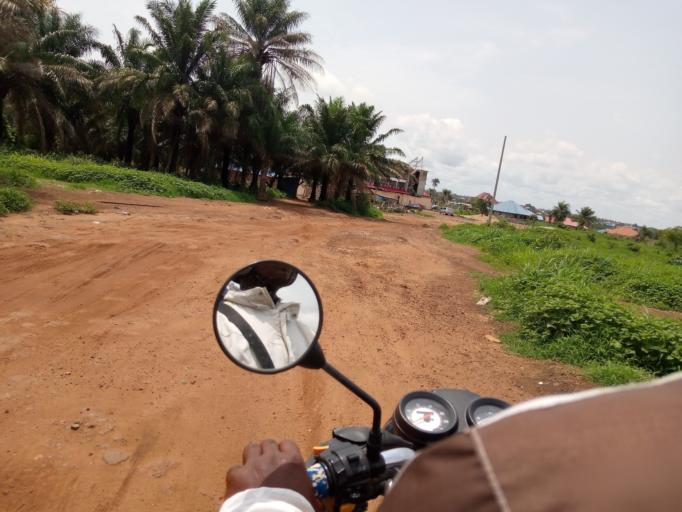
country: SL
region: Western Area
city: Waterloo
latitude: 8.3730
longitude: -13.0872
